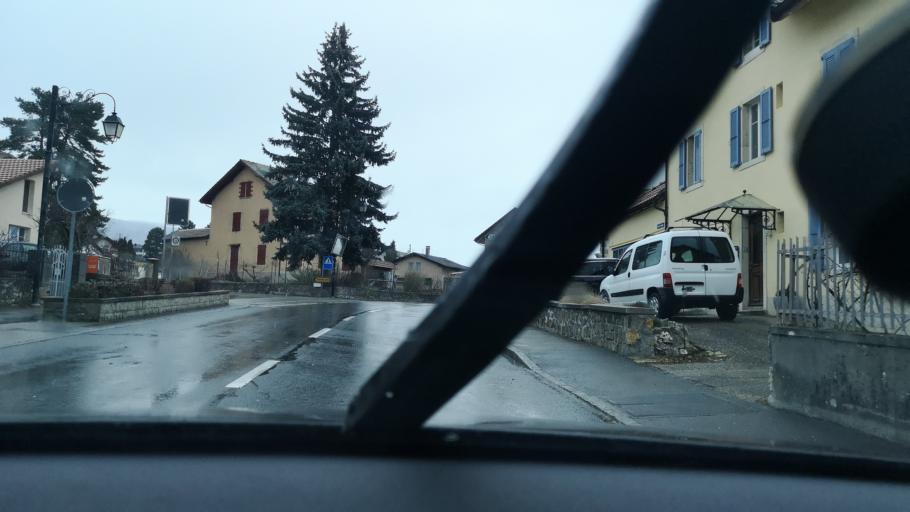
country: CH
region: Neuchatel
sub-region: Boudry District
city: Bevaix
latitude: 46.9321
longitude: 6.8155
